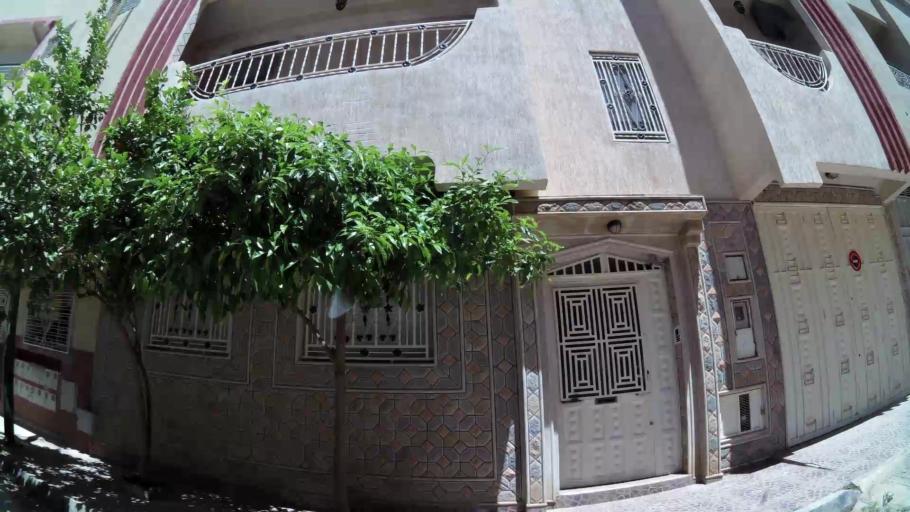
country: MA
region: Meknes-Tafilalet
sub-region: Meknes
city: Meknes
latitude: 33.8644
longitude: -5.5743
